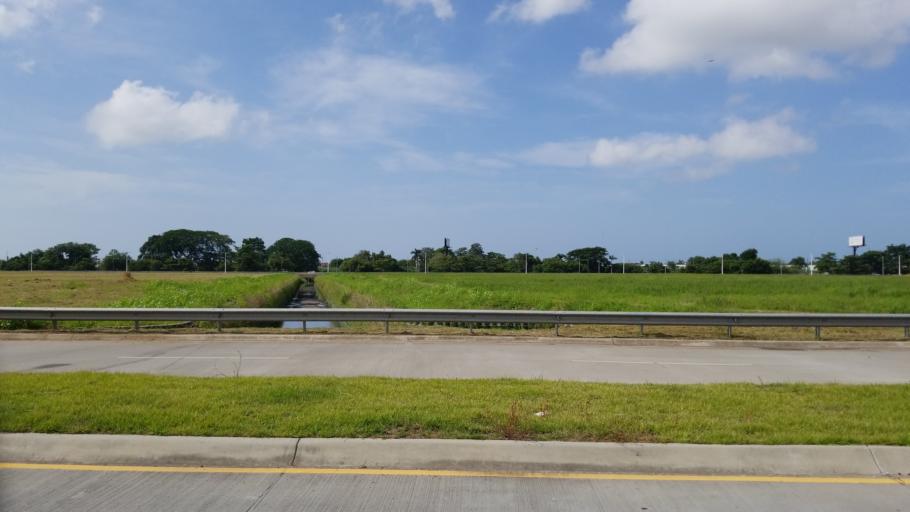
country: PA
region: Panama
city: San Miguelito
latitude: 9.0396
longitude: -79.4278
